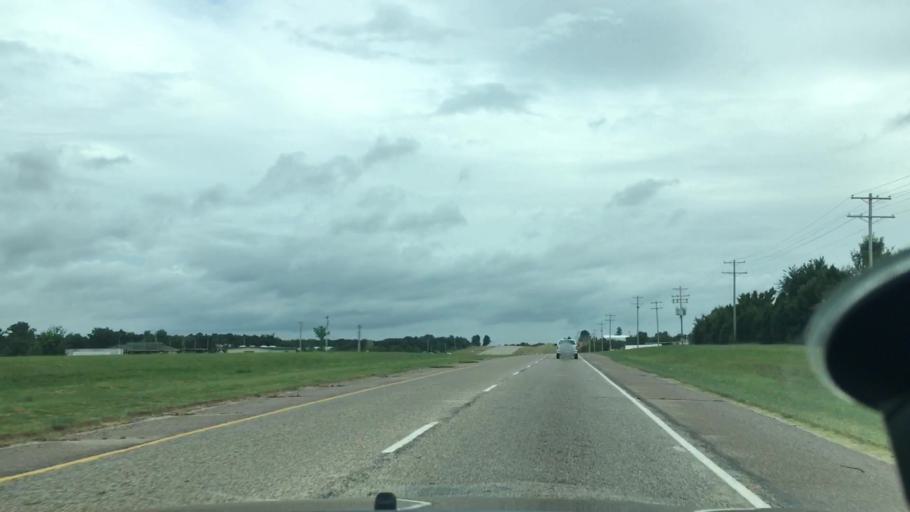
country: US
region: Oklahoma
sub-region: Seminole County
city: Seminole
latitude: 35.2812
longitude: -96.6712
